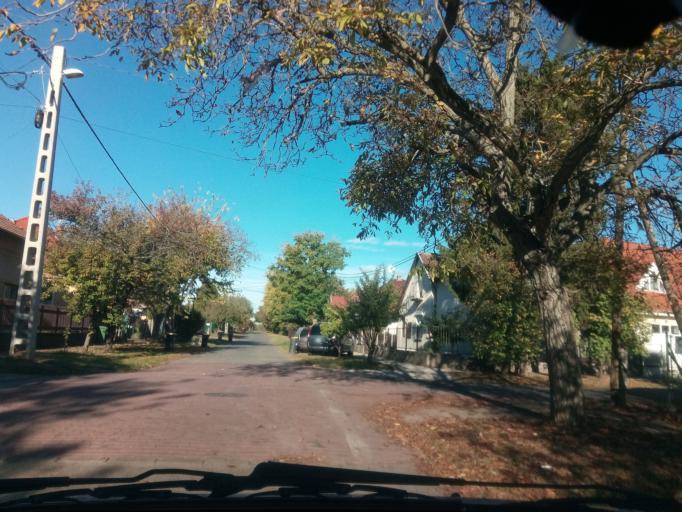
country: HU
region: Budapest
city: Budapest XVIII. keruelet
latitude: 47.4346
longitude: 19.2180
